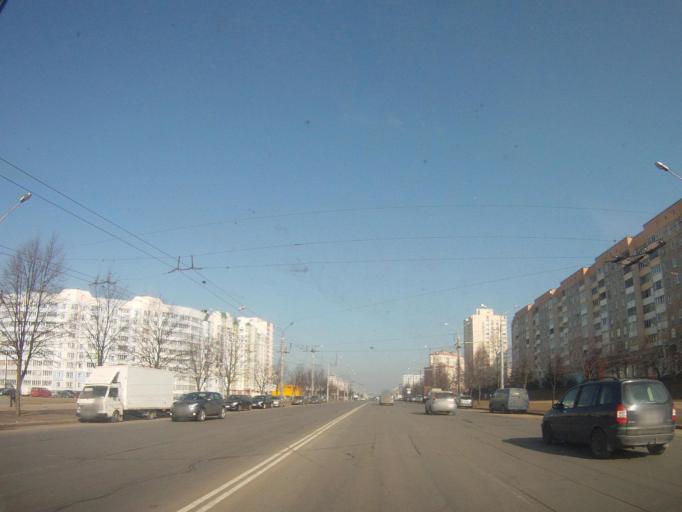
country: BY
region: Minsk
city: Novoye Medvezhino
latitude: 53.9017
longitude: 27.4353
